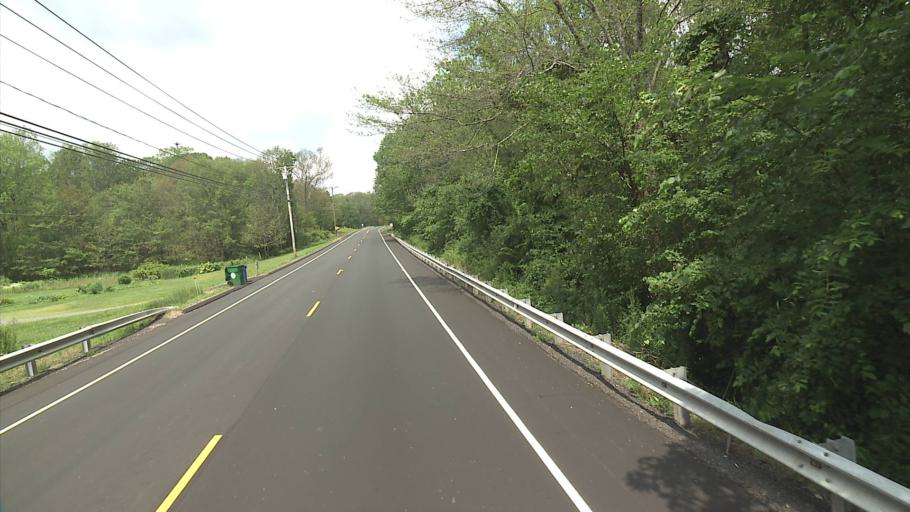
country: US
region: Connecticut
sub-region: New London County
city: Preston City
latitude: 41.5759
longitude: -71.8846
